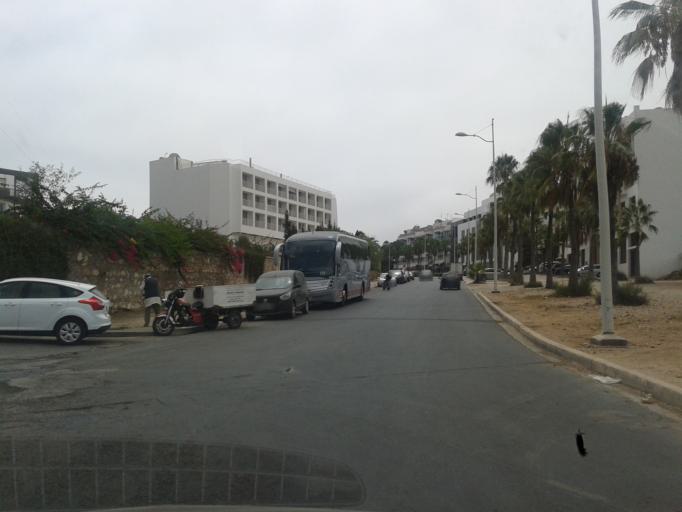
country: MA
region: Souss-Massa-Draa
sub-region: Agadir-Ida-ou-Tnan
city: Agadir
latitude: 30.4250
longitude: -9.6062
